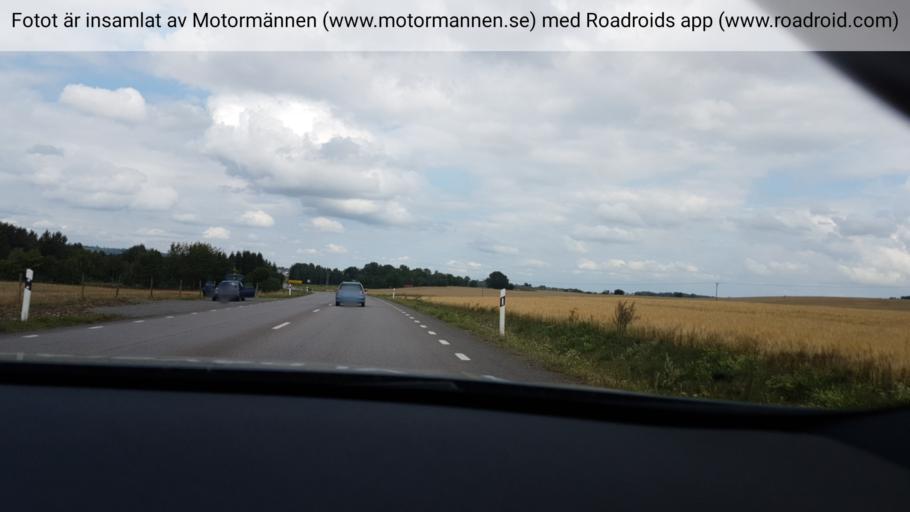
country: SE
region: Vaestra Goetaland
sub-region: Falkopings Kommun
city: Falkoeping
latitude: 58.1380
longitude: 13.5632
